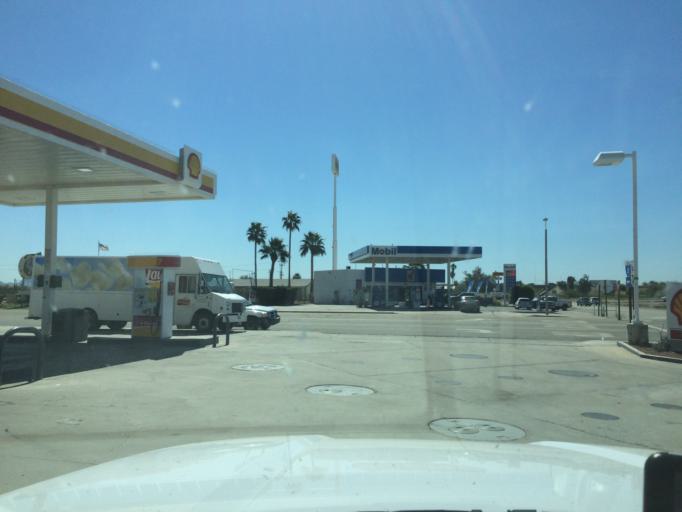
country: US
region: California
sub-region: Riverside County
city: Blythe
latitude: 33.6111
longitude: -114.5705
